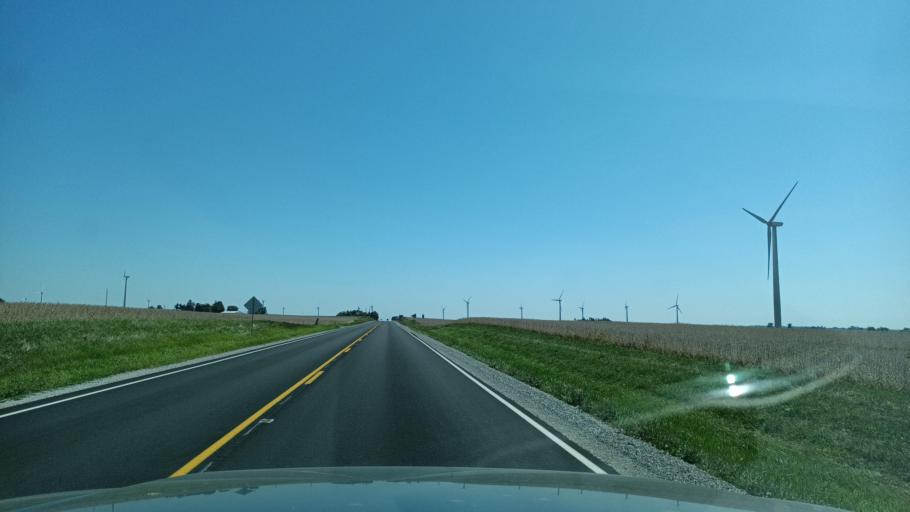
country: US
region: Illinois
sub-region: McLean County
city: Danvers
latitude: 40.5822
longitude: -89.1026
